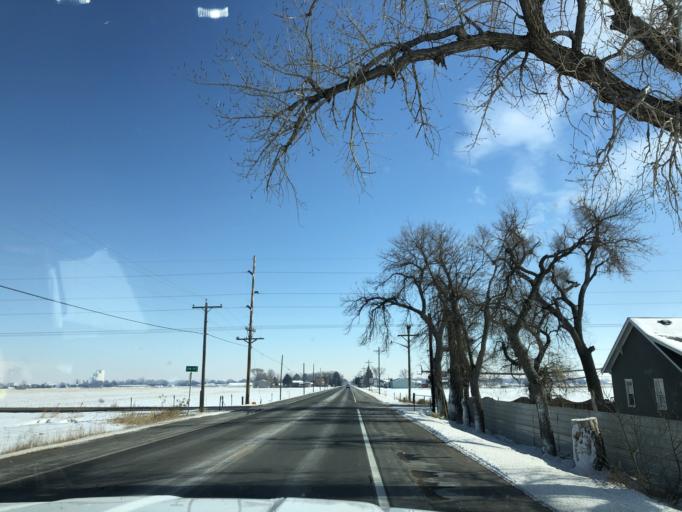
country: US
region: Colorado
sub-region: Morgan County
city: Fort Morgan
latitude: 40.2540
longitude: -103.8306
